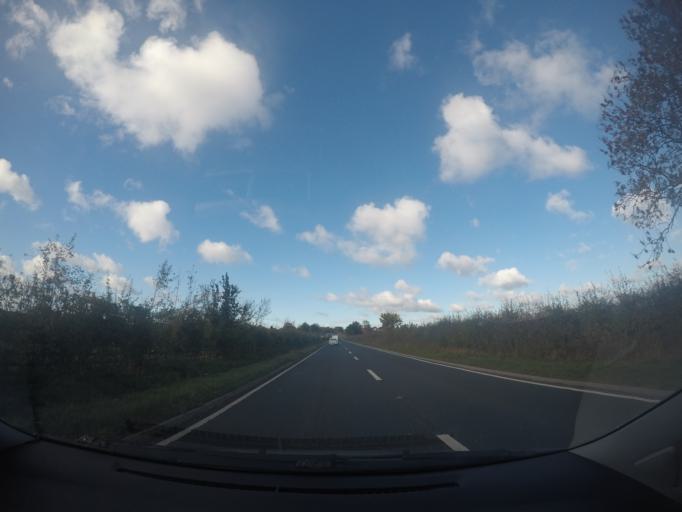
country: GB
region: England
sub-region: City and Borough of Leeds
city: Walton
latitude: 54.0011
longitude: -1.2901
